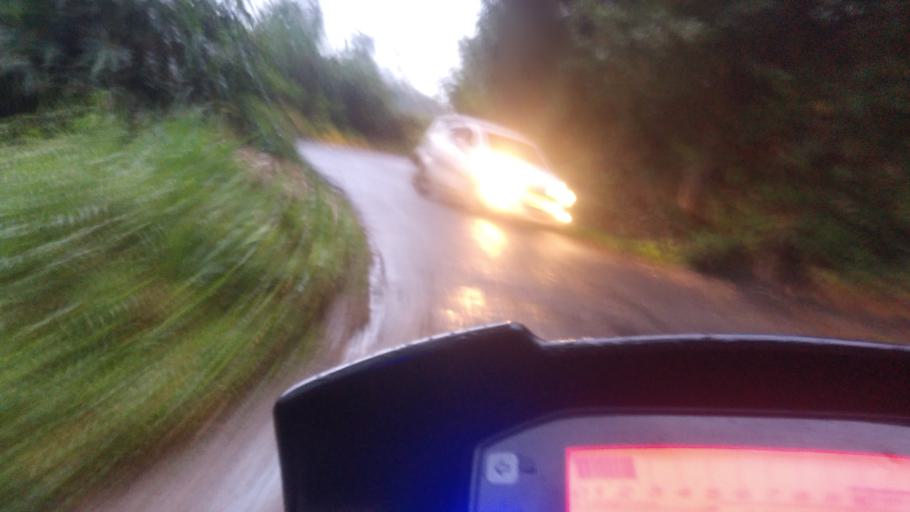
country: IN
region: Kerala
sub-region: Kottayam
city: Erattupetta
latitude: 9.5491
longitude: 76.9710
